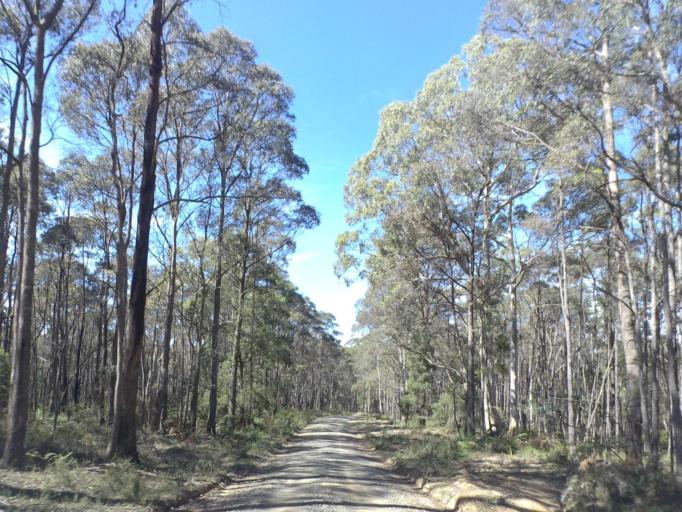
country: AU
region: Victoria
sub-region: Moorabool
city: Bacchus Marsh
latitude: -37.4057
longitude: 144.3265
